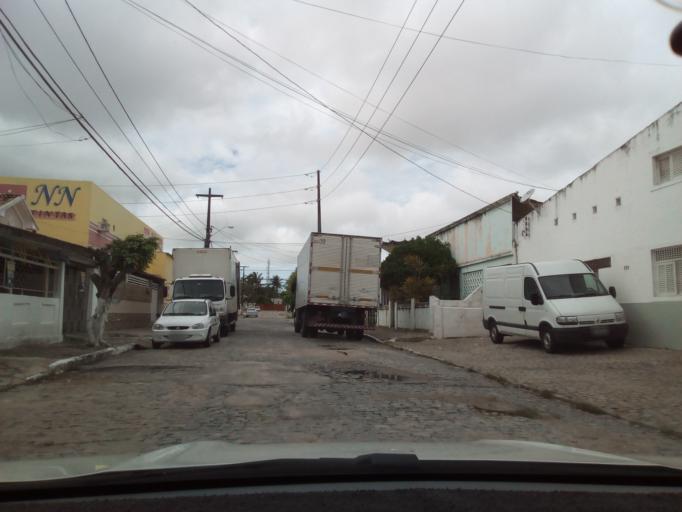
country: BR
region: Paraiba
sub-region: Joao Pessoa
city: Joao Pessoa
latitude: -7.1225
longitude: -34.8639
